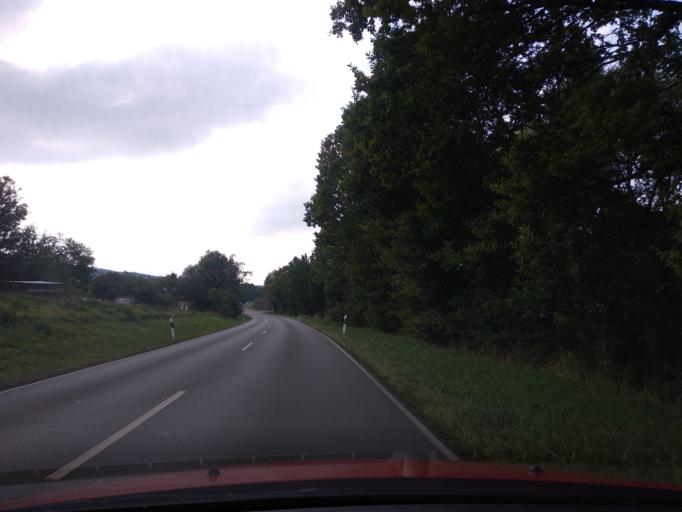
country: DE
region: Hesse
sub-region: Regierungsbezirk Kassel
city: Calden
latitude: 51.3705
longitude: 9.3951
